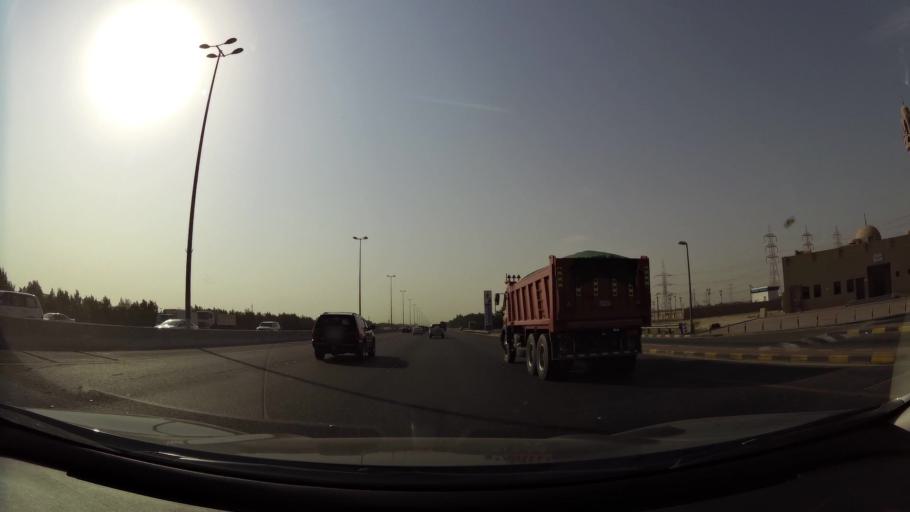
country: KW
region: Al Ahmadi
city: Ar Riqqah
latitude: 29.1159
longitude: 48.0941
